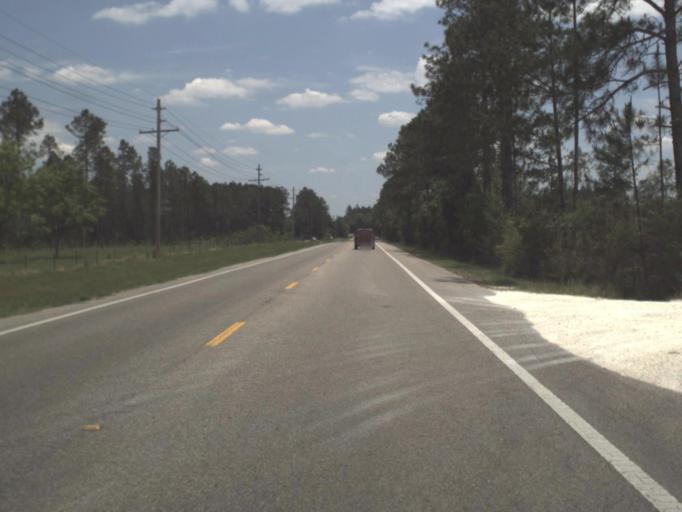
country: US
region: Florida
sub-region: Calhoun County
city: Blountstown
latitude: 30.4686
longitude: -85.0826
